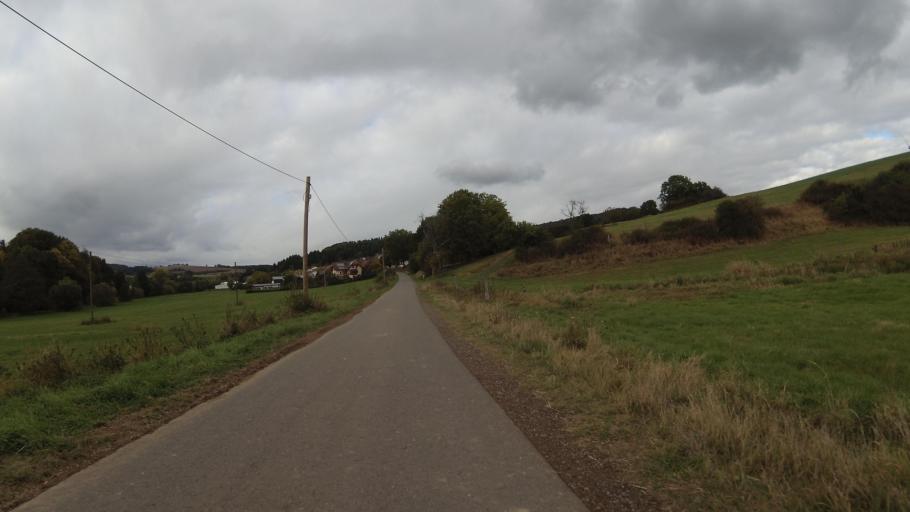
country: DE
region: Rheinland-Pfalz
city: Ohmbach
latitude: 49.4646
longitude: 7.3498
